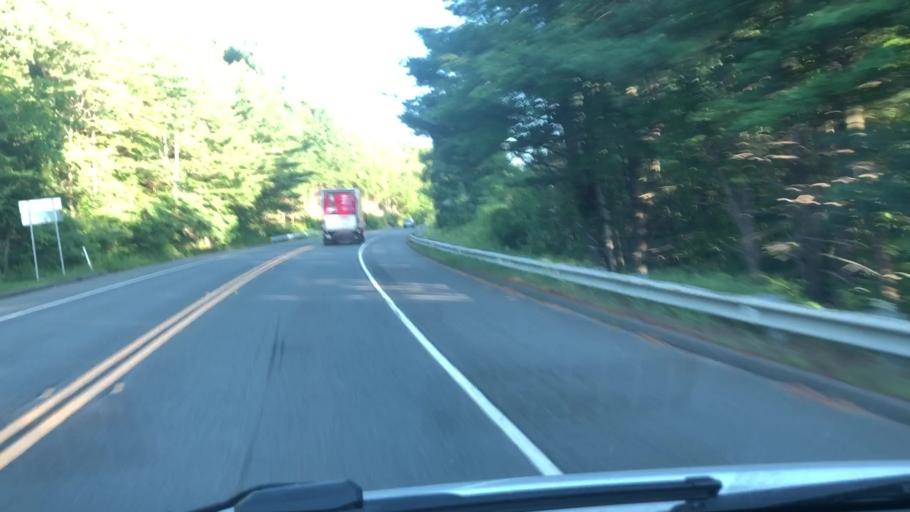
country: US
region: Massachusetts
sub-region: Hampshire County
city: Chesterfield
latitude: 42.4575
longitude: -72.8919
